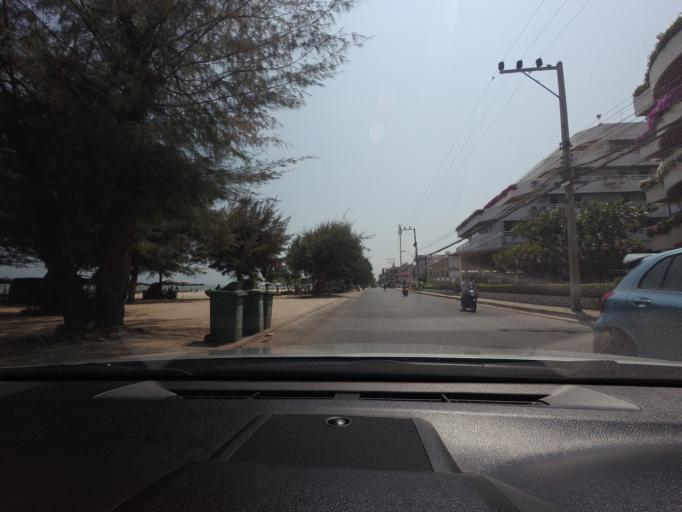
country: TH
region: Phetchaburi
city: Cha-am
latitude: 12.8050
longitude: 99.9878
